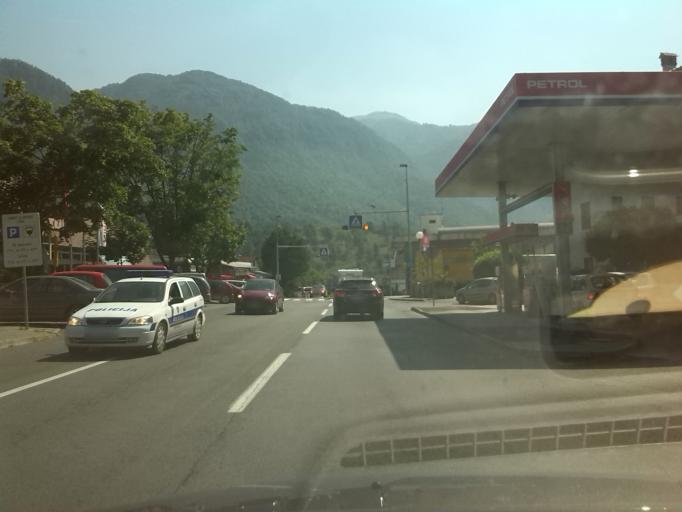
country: SI
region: Tolmin
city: Tolmin
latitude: 46.1828
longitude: 13.7338
